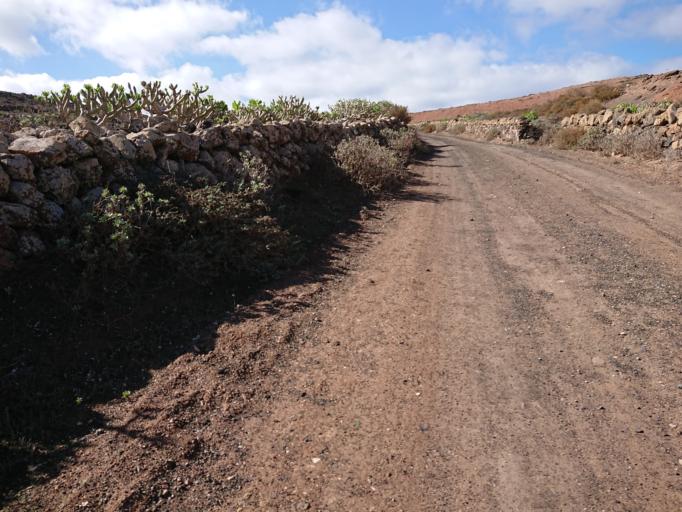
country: ES
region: Canary Islands
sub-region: Provincia de Las Palmas
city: Haria
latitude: 29.1456
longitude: -13.5172
